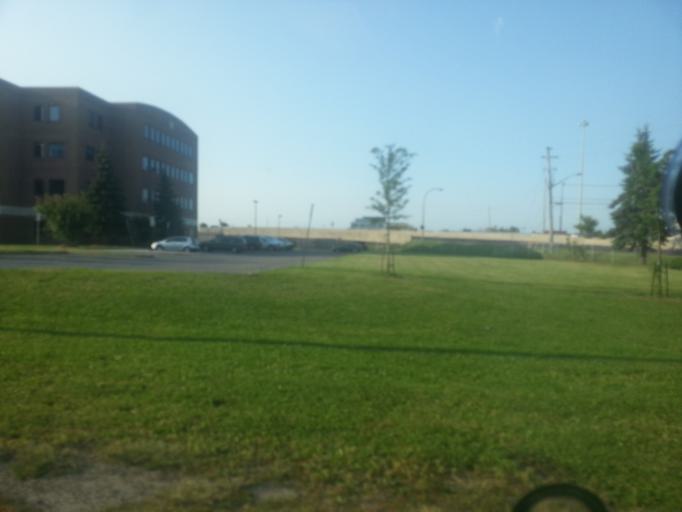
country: CA
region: Ontario
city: Ottawa
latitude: 45.4219
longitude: -75.6339
